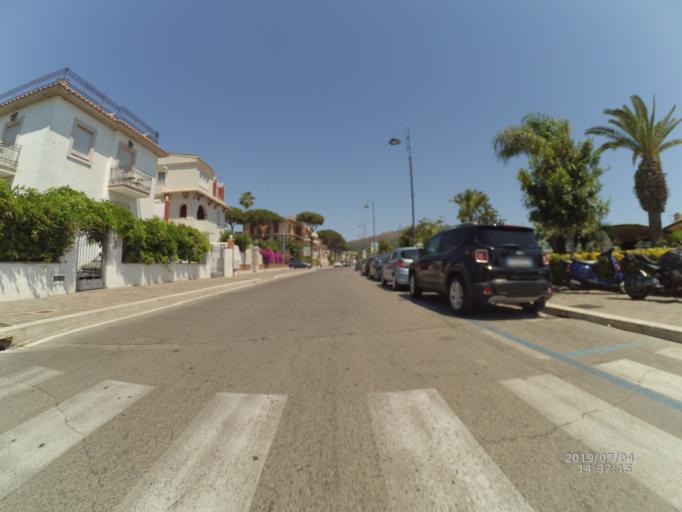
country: IT
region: Latium
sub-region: Provincia di Latina
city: Gaeta
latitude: 41.2119
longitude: 13.5601
